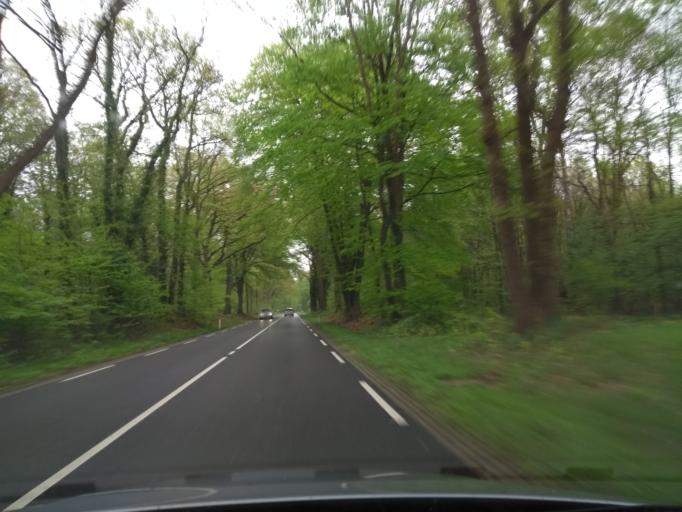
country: DE
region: Lower Saxony
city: Getelo
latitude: 52.4014
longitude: 6.8594
